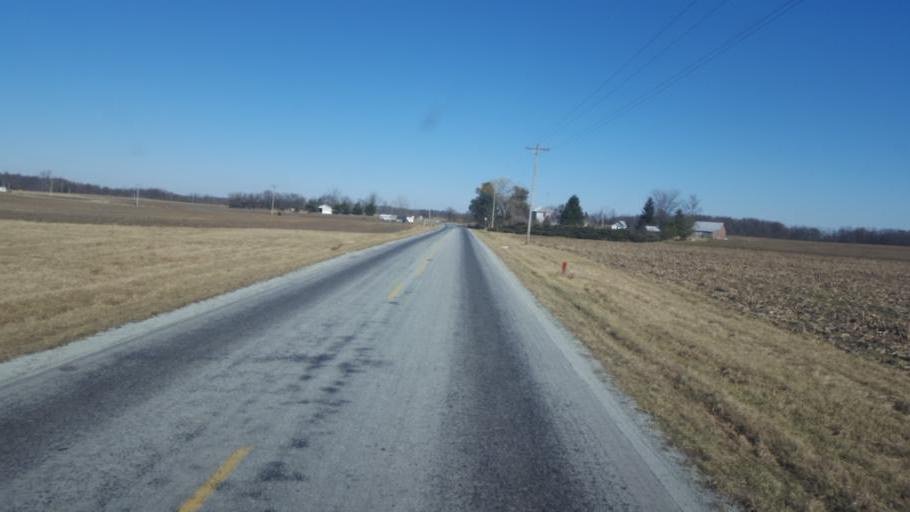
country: US
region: Ohio
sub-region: Hardin County
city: Kenton
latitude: 40.6374
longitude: -83.4784
